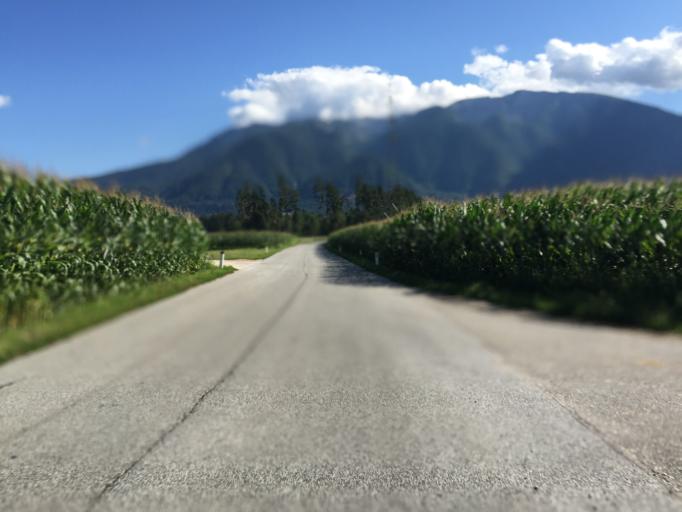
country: AT
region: Carinthia
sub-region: Politischer Bezirk Volkermarkt
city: Feistritz ob Bleiburg
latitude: 46.5696
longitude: 14.7704
